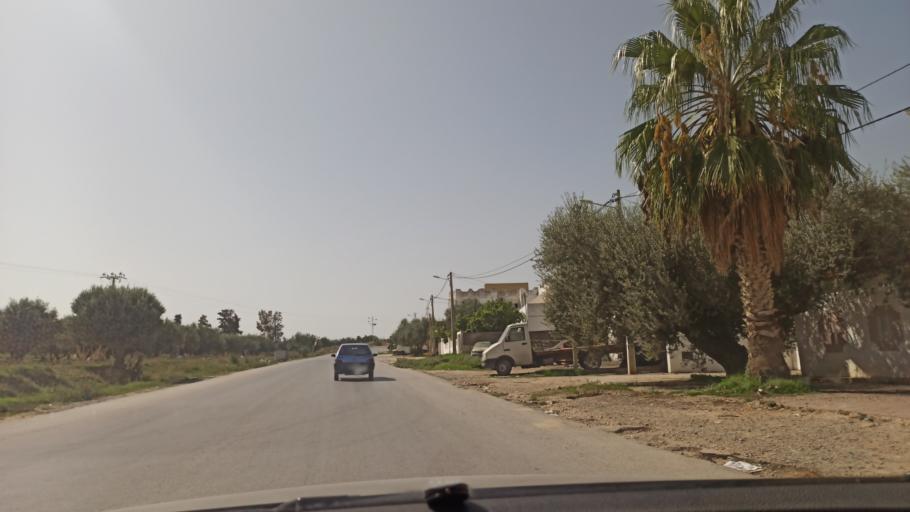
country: TN
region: Manouba
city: Manouba
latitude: 36.7515
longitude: 10.1004
